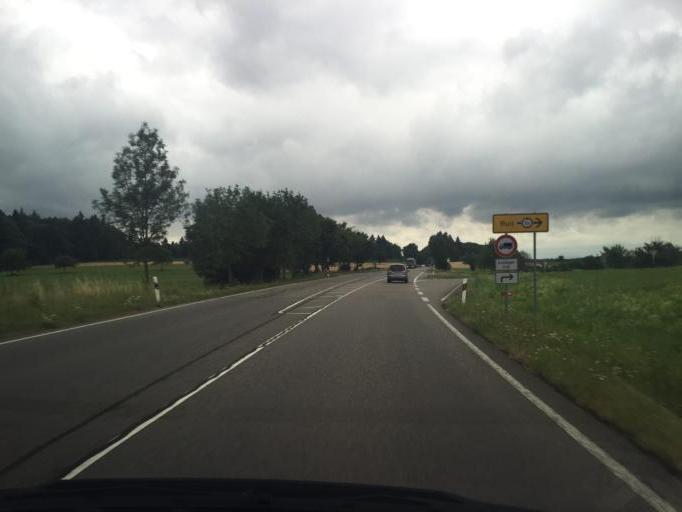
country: DE
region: Baden-Wuerttemberg
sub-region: Karlsruhe Region
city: Bretten
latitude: 48.9999
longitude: 8.7177
